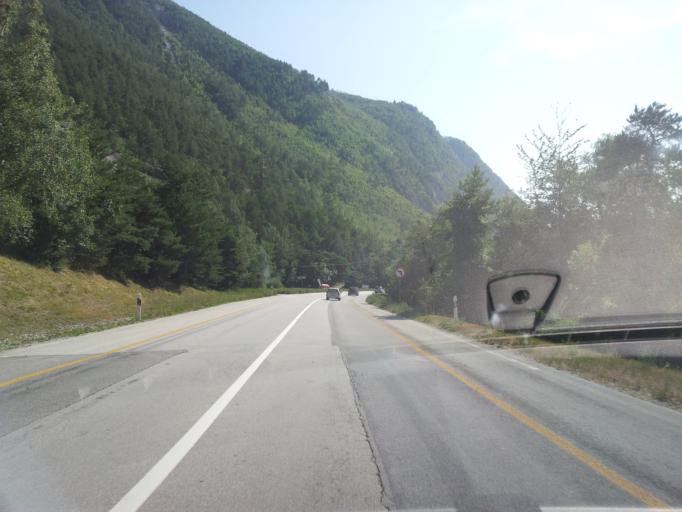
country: CH
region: Valais
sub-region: Leuk District
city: Salgesch
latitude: 46.2957
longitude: 7.5862
